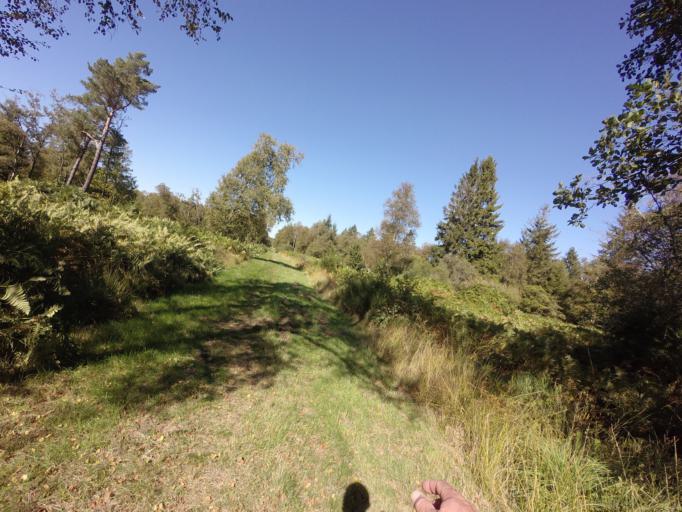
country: DE
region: North Rhine-Westphalia
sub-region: Regierungsbezirk Koln
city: Roetgen
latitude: 50.6014
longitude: 6.1715
